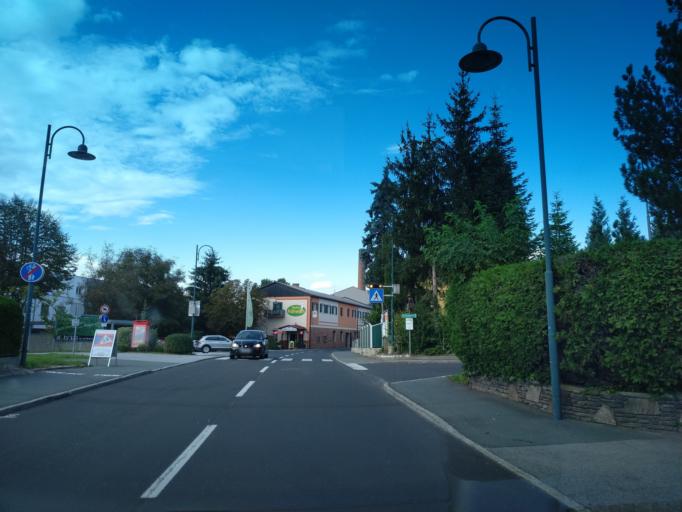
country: AT
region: Styria
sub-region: Politischer Bezirk Leibnitz
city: Kaindorf an der Sulm
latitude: 46.7914
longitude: 15.5333
